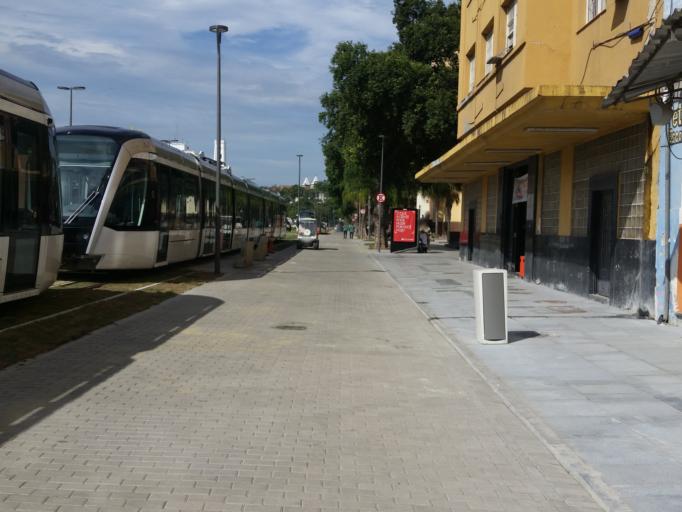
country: BR
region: Rio de Janeiro
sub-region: Rio De Janeiro
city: Rio de Janeiro
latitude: -22.8951
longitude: -43.1848
